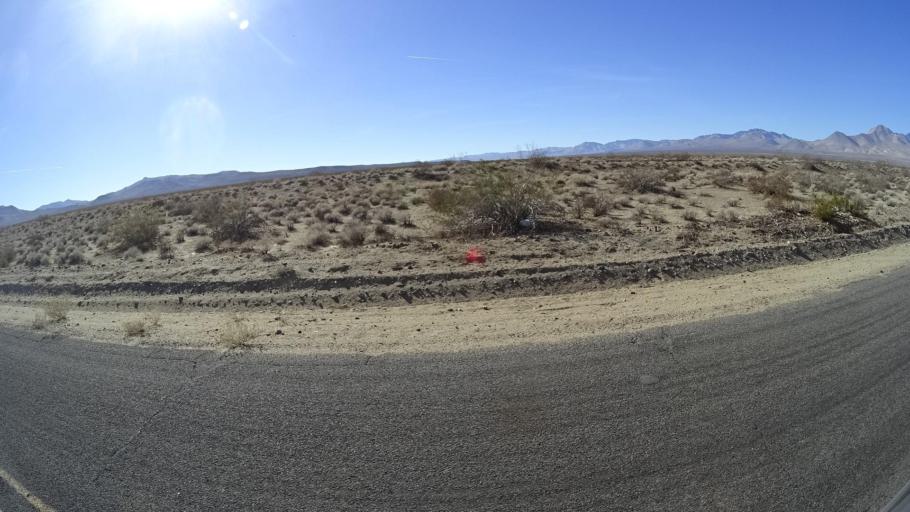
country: US
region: California
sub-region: Kern County
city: China Lake Acres
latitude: 35.5833
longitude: -117.7888
